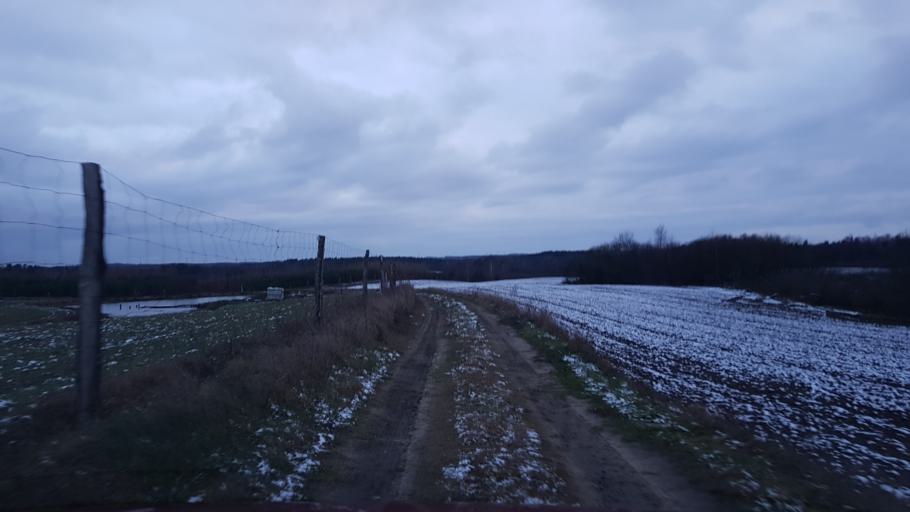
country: PL
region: Pomeranian Voivodeship
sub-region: Powiat bytowski
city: Tuchomie
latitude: 54.1490
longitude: 17.3036
